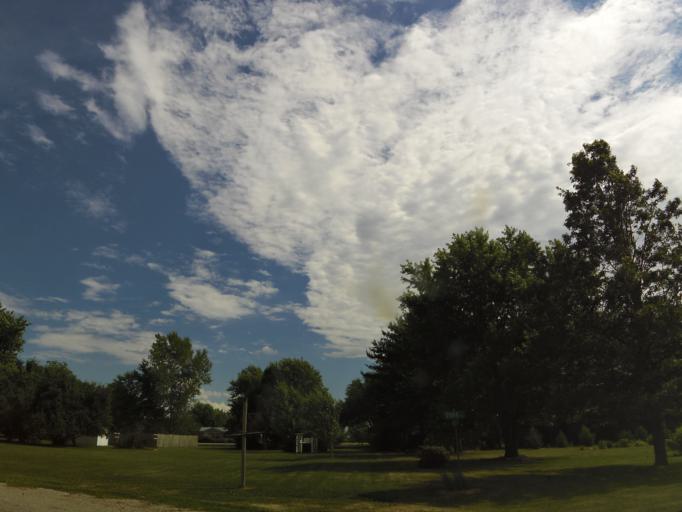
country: US
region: Iowa
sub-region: Henry County
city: Winfield
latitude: 41.1043
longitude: -91.5484
